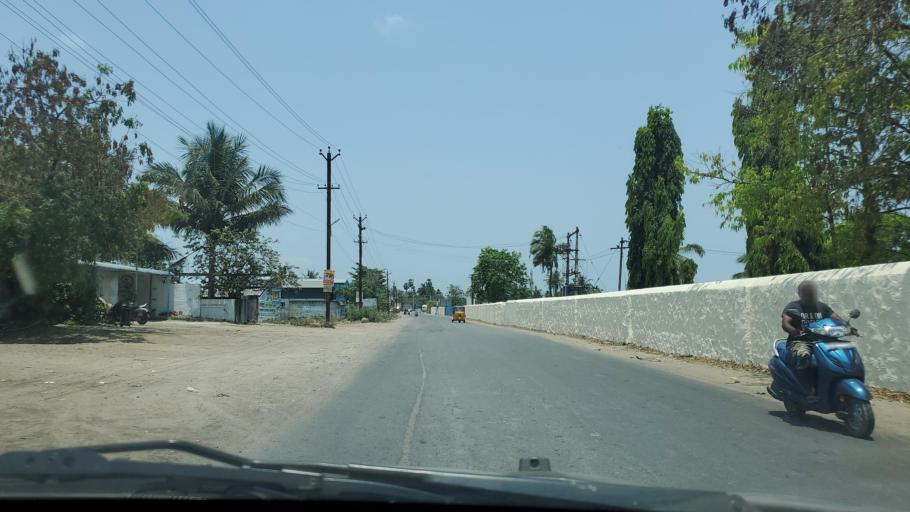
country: IN
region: Tamil Nadu
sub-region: Kancheepuram
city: Vengavasal
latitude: 12.8513
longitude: 80.1710
